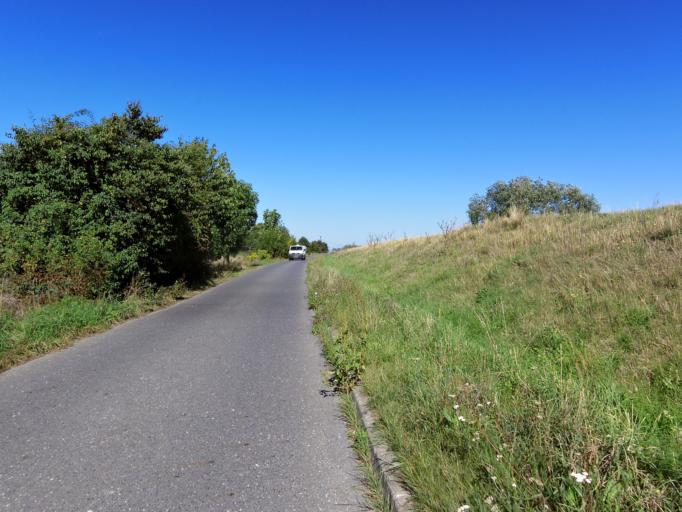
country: DE
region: Saxony
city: Dommitzsch
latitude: 51.6465
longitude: 12.8973
